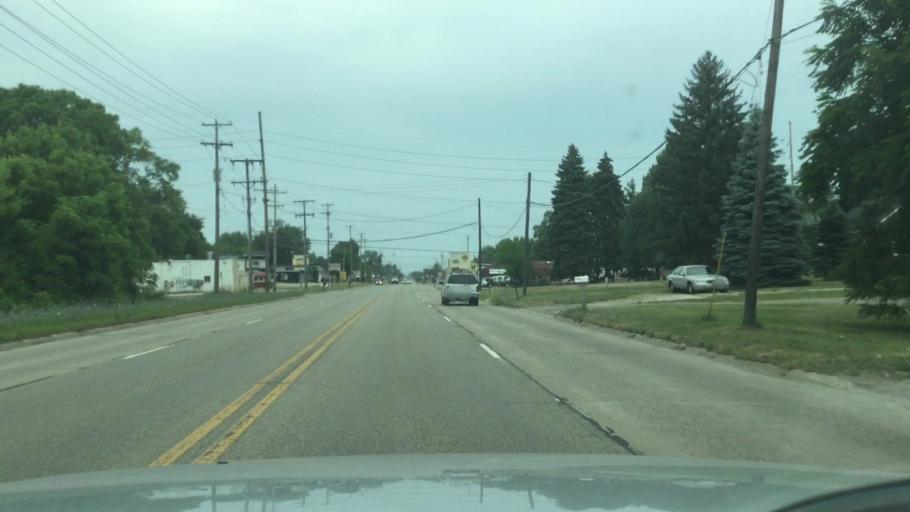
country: US
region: Michigan
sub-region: Genesee County
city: Flint
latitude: 42.9659
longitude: -83.6927
